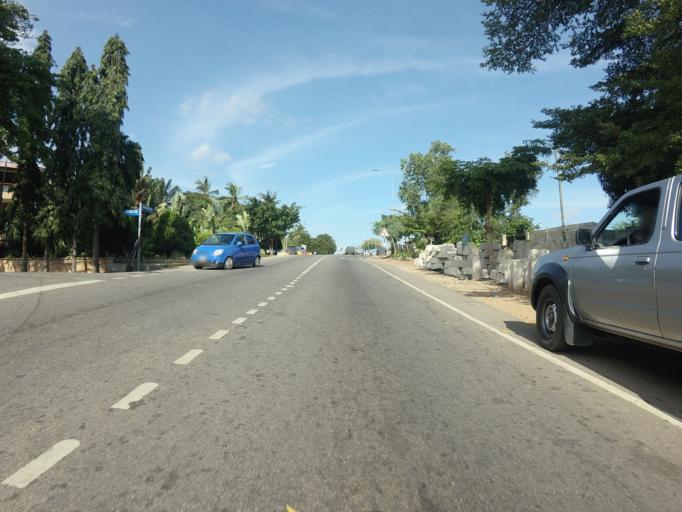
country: GH
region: Greater Accra
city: Medina Estates
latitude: 5.6302
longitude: -0.1595
